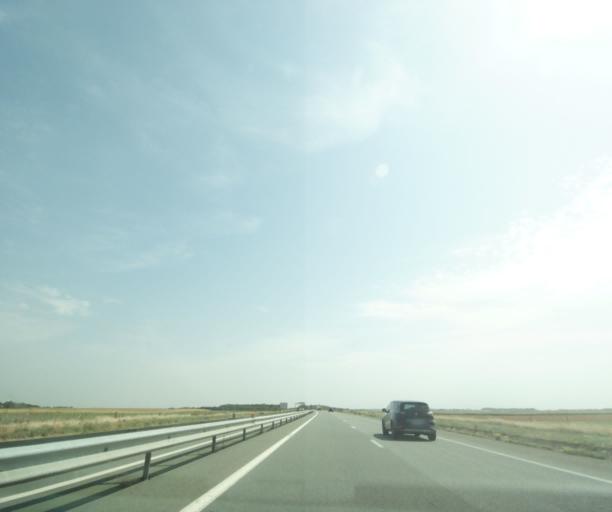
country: FR
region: Pays de la Loire
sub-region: Departement de la Vendee
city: Fontenay-le-Comte
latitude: 46.4229
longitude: -0.7811
